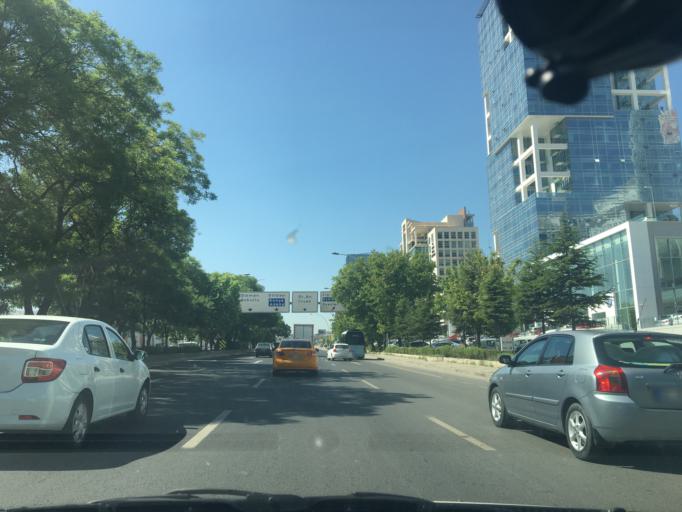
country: TR
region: Ankara
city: Ankara
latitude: 39.8922
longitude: 32.8128
